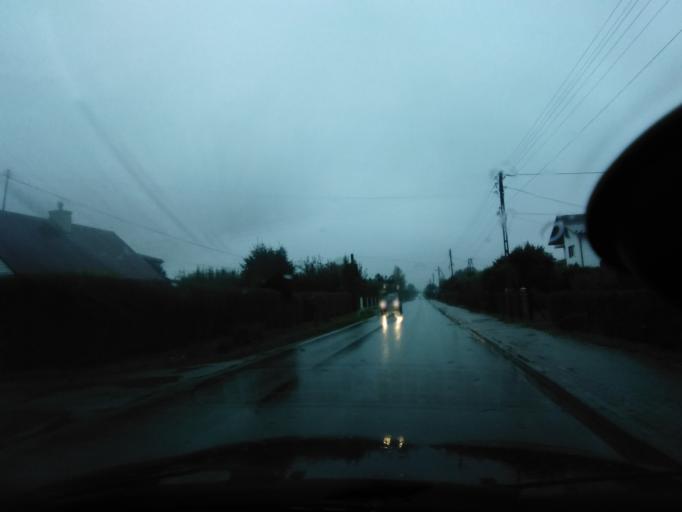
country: PL
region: Subcarpathian Voivodeship
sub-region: Powiat krosnienski
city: Miejsce Piastowe
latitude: 49.6555
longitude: 21.8060
